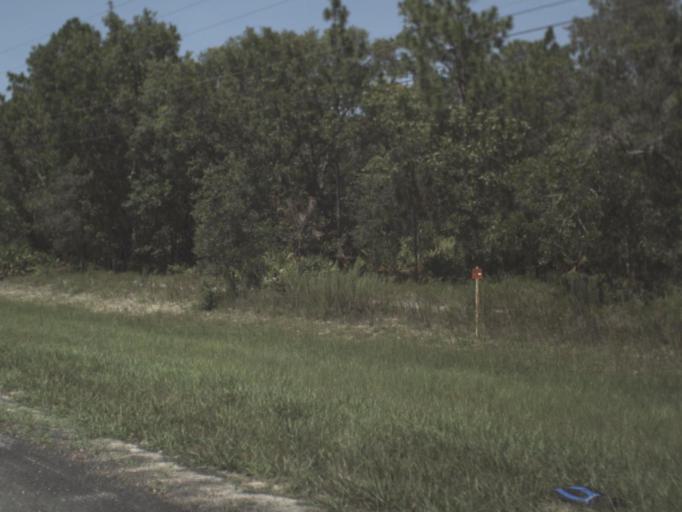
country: US
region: Florida
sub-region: Citrus County
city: Sugarmill Woods
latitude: 28.6624
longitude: -82.5521
